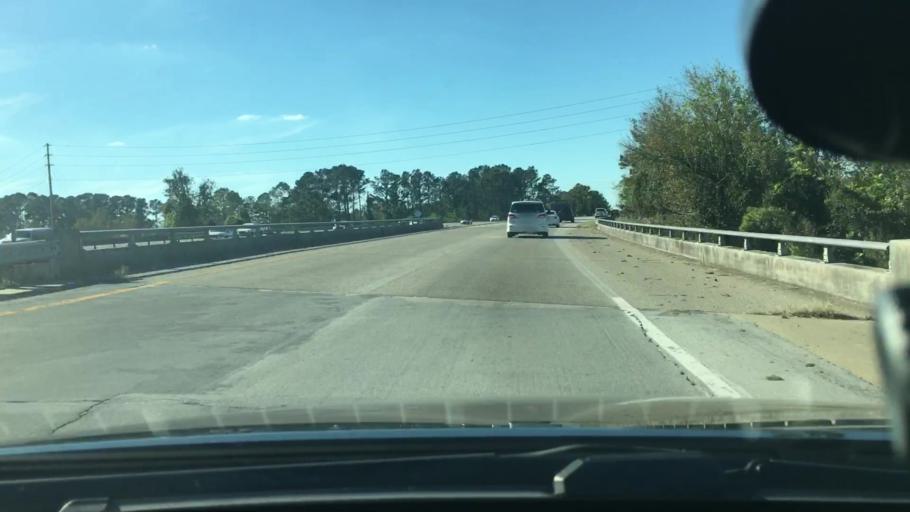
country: US
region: North Carolina
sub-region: Craven County
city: Trent Woods
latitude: 35.1002
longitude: -77.0777
